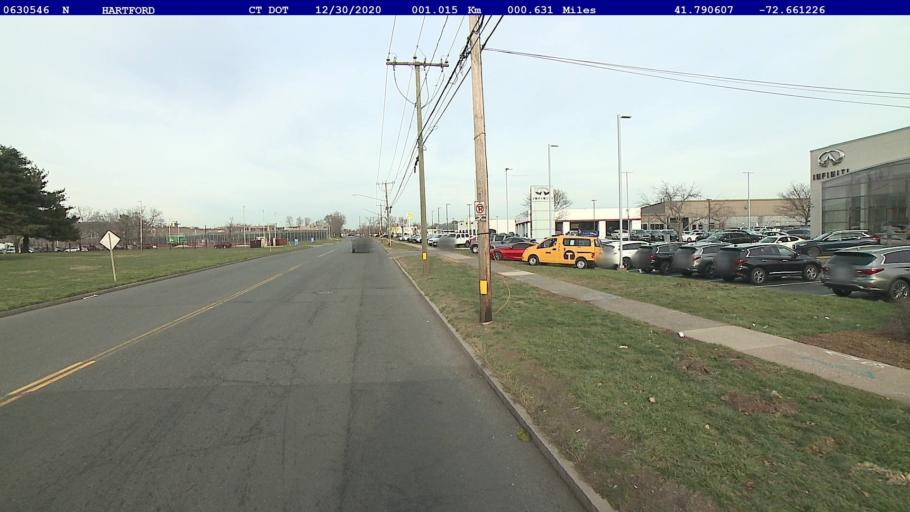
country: US
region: Connecticut
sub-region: Hartford County
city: Hartford
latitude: 41.7906
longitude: -72.6612
